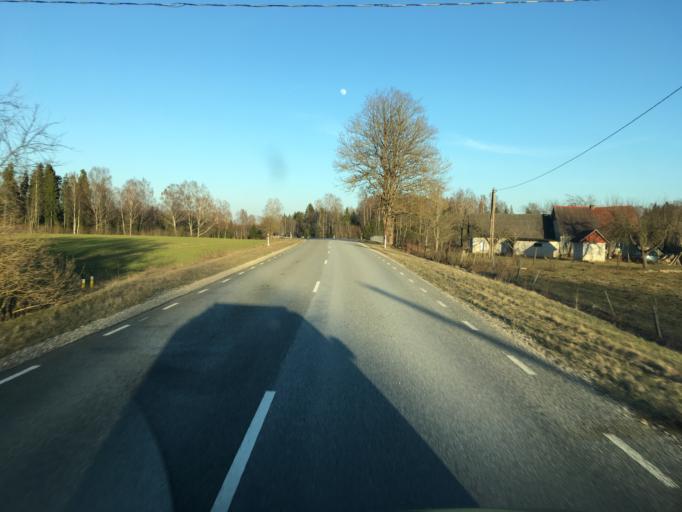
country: EE
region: Raplamaa
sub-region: Rapla vald
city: Rapla
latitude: 59.0763
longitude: 24.8702
